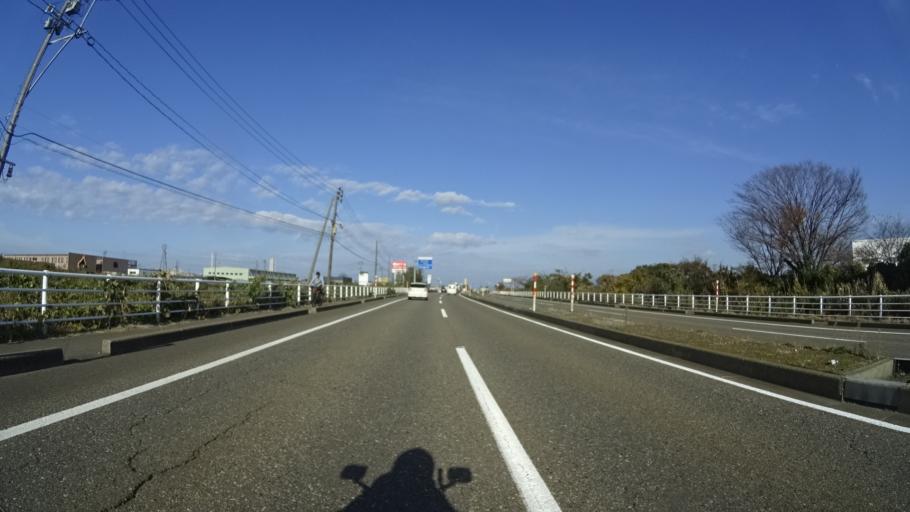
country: JP
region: Niigata
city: Joetsu
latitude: 37.1880
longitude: 138.2739
